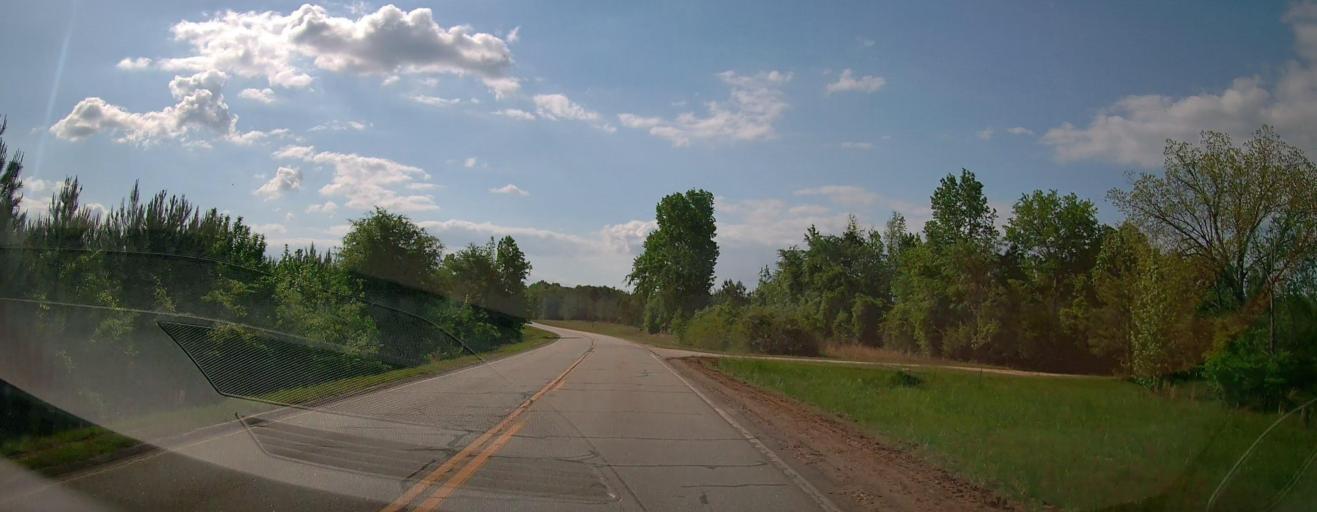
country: US
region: Georgia
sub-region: Washington County
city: Tennille
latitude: 32.9158
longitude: -82.9902
